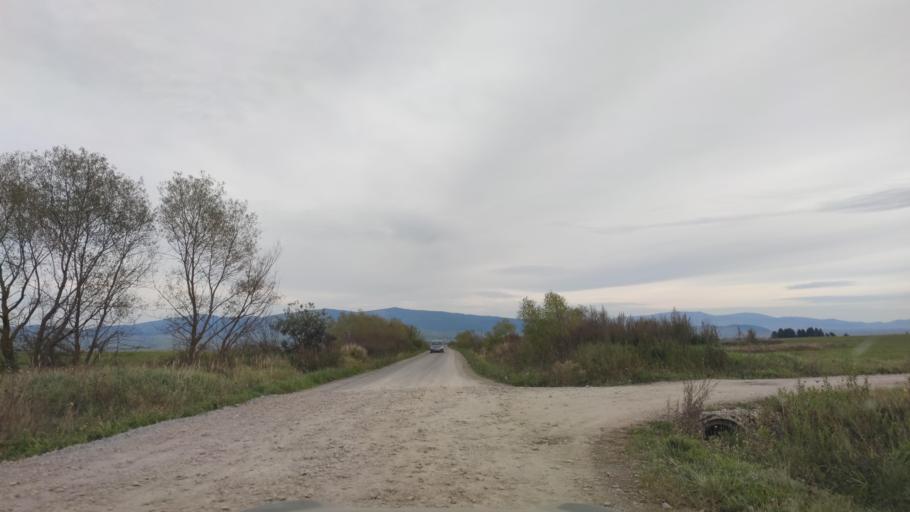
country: RO
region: Harghita
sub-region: Comuna Remetea
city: Remetea
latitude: 46.8081
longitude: 25.4073
